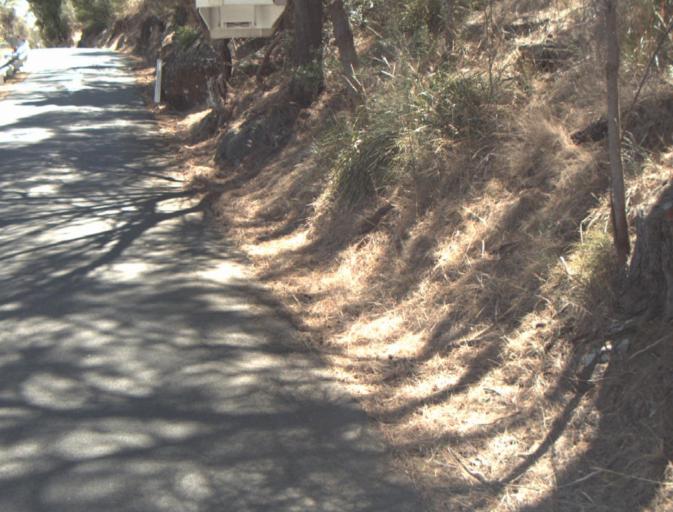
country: AU
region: Tasmania
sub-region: Launceston
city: West Launceston
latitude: -41.4556
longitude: 147.1181
